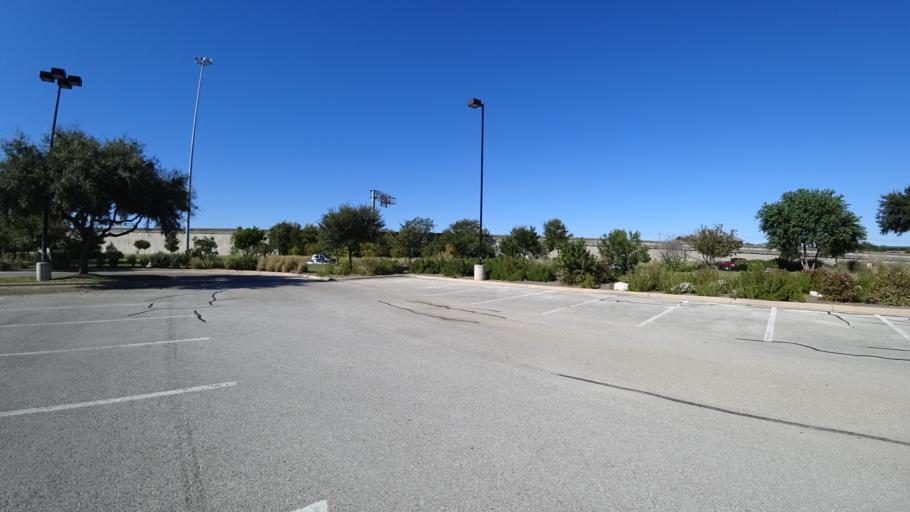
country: US
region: Texas
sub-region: Travis County
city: Rollingwood
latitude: 30.2321
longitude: -97.8152
